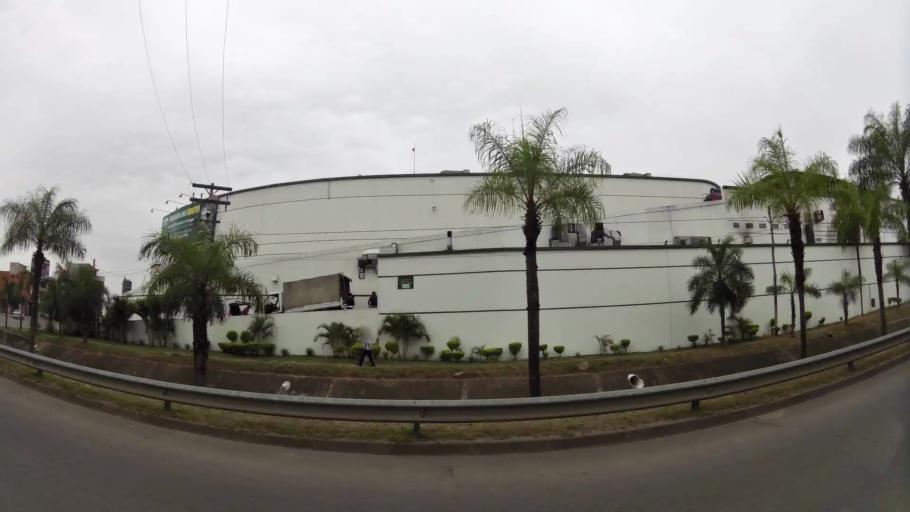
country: BO
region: Santa Cruz
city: Santa Cruz de la Sierra
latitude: -17.7727
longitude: -63.2044
